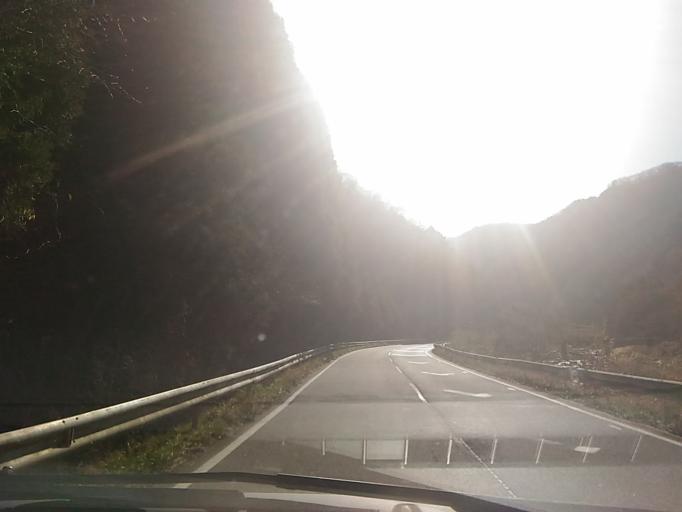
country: JP
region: Fukushima
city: Ishikawa
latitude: 37.0339
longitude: 140.6484
